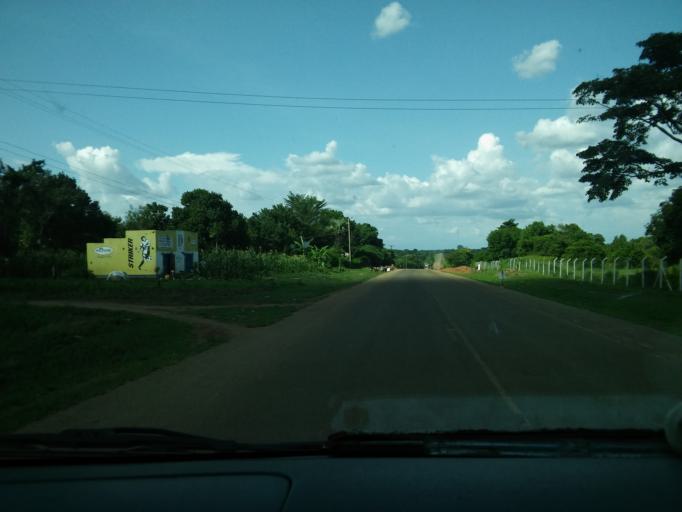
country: UG
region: Eastern Region
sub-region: Kibuku District
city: Kibuku
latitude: 1.0066
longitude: 33.7783
